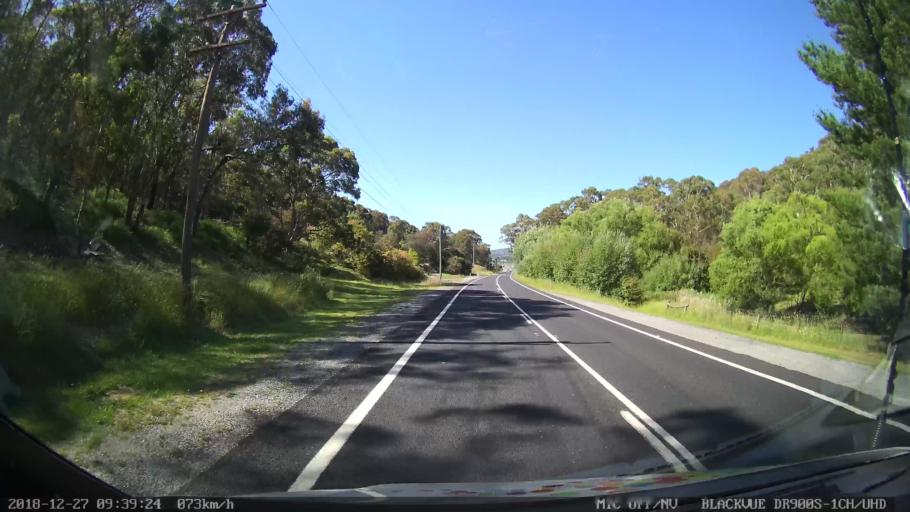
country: AU
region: New South Wales
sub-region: Lithgow
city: Portland
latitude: -33.2923
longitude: 150.0352
